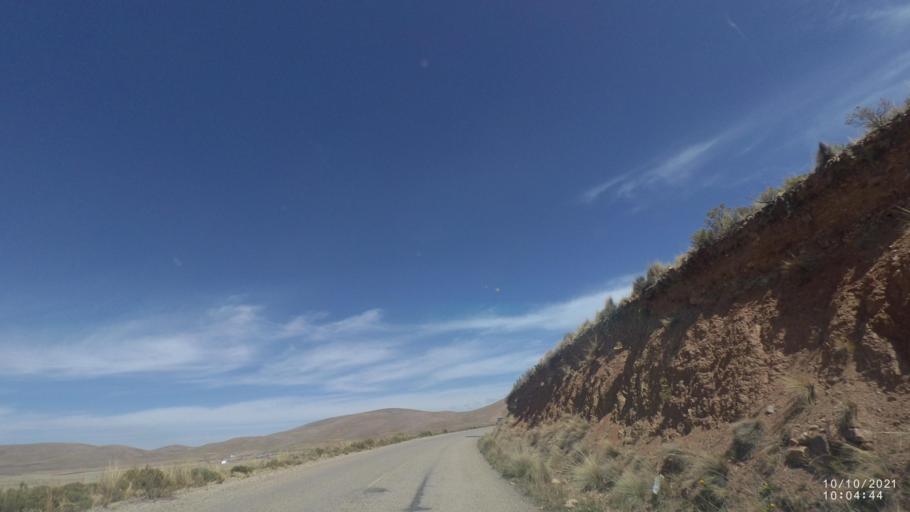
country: BO
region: La Paz
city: Eucaliptus
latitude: -17.3821
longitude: -67.4503
